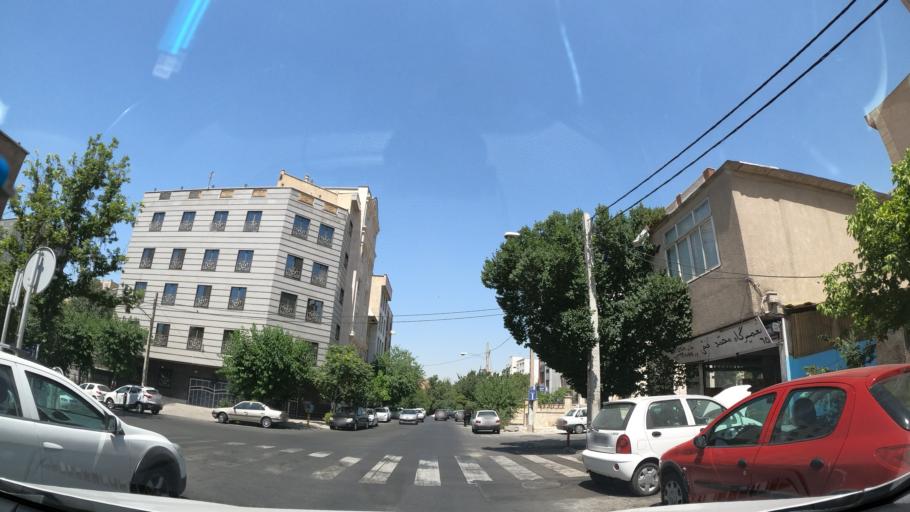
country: IR
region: Tehran
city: Tehran
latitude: 35.7272
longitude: 51.3716
